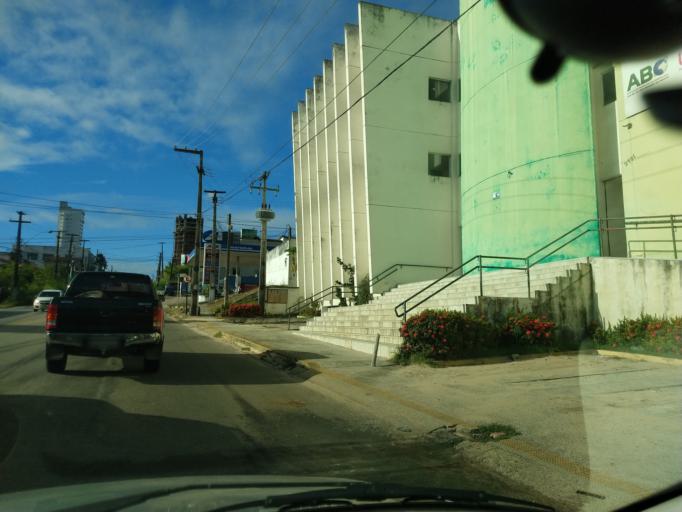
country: BR
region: Rio Grande do Norte
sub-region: Natal
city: Natal
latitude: -5.8323
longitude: -35.2231
